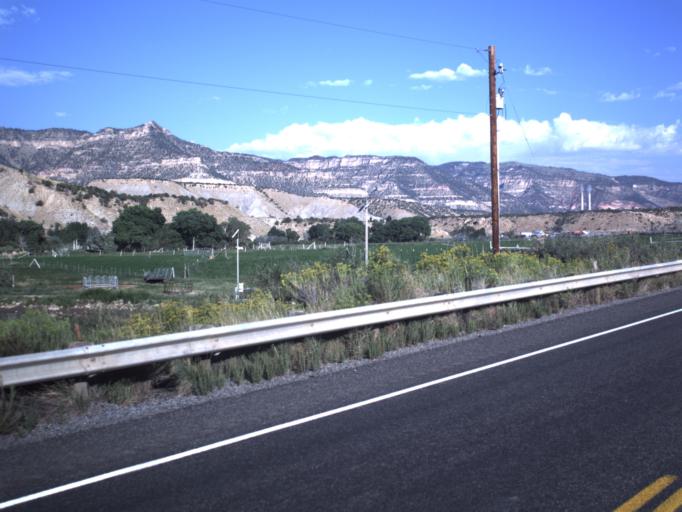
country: US
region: Utah
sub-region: Emery County
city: Huntington
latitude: 39.3585
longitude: -111.0303
